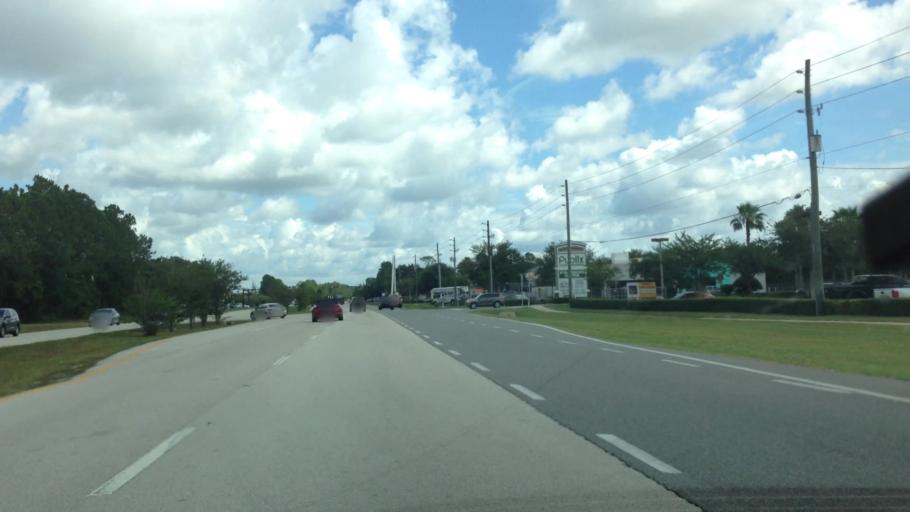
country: US
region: Florida
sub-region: Saint Johns County
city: Ponte Vedra Beach
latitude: 30.2540
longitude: -81.4664
